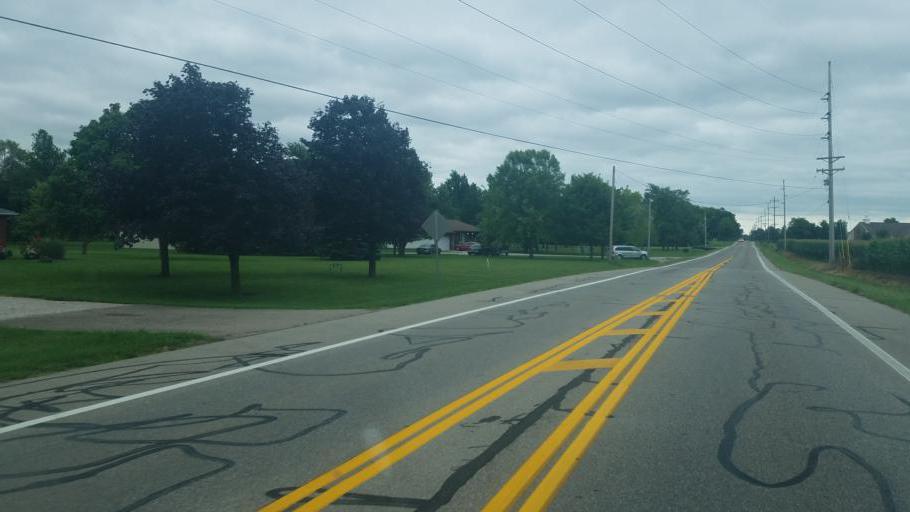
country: US
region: Ohio
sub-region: Pickaway County
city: Commercial Point
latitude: 39.7679
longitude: -83.0256
